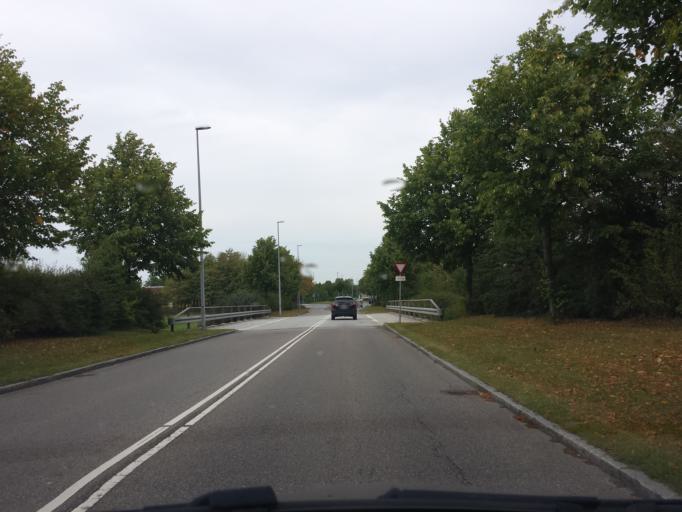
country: DK
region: Capital Region
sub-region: Hoje-Taastrup Kommune
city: Taastrup
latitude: 55.6495
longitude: 12.2662
